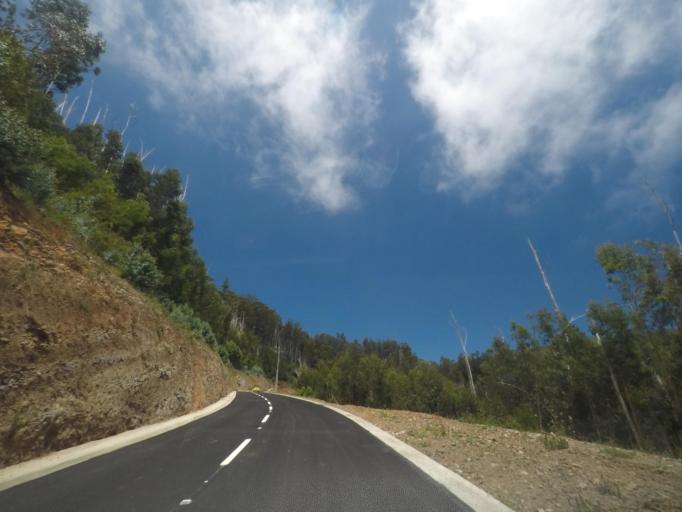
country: PT
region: Madeira
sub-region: Calheta
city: Arco da Calheta
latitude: 32.7513
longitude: -17.1526
